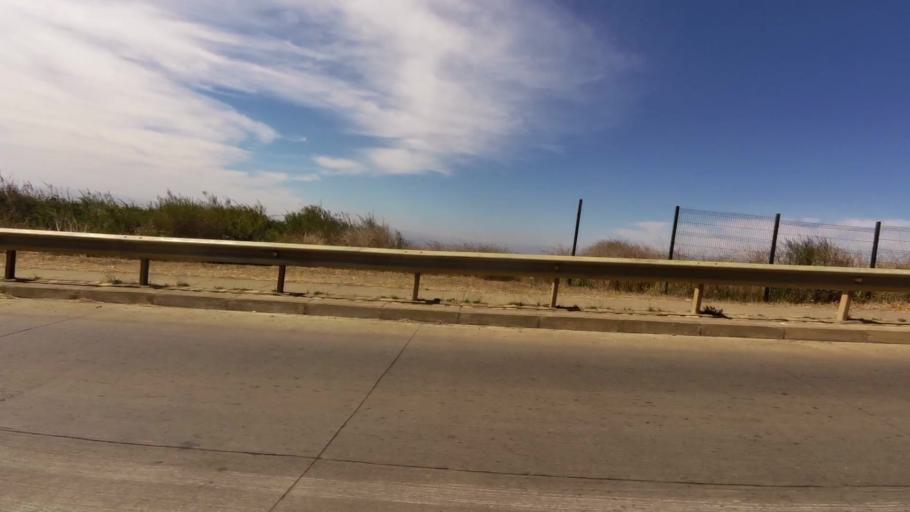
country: CL
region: Biobio
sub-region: Provincia de Concepcion
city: Talcahuano
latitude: -36.7103
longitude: -73.1239
